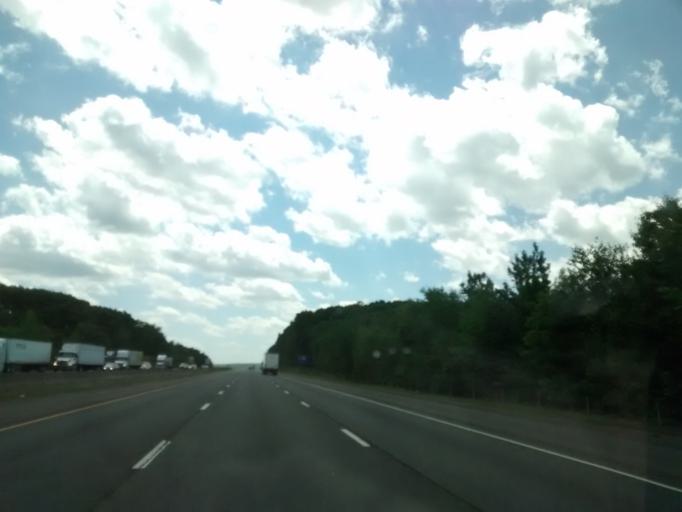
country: US
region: Connecticut
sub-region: Tolland County
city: Tolland
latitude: 41.8752
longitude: -72.3364
